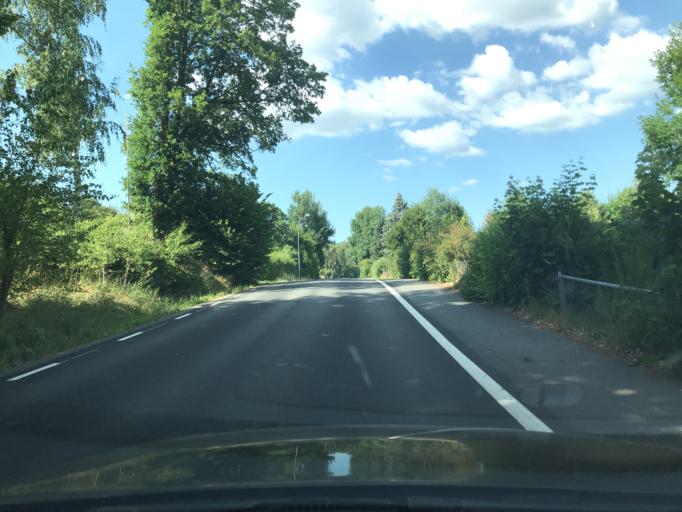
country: SE
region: Skane
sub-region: Hassleholms Kommun
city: Hastveda
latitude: 56.2822
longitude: 13.9146
